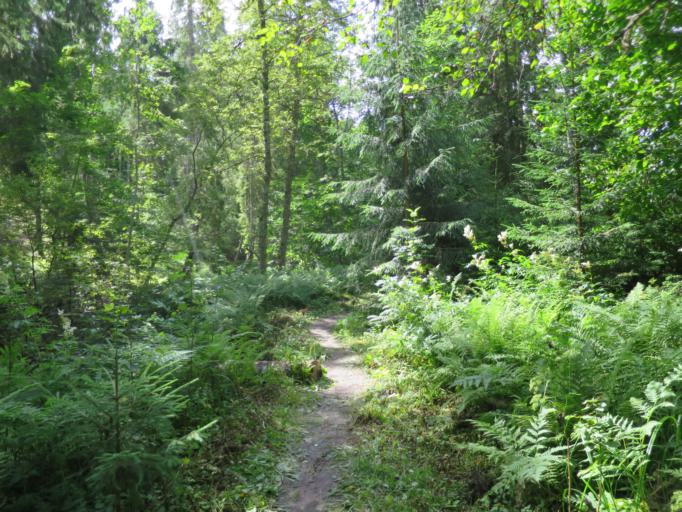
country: LV
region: Ligatne
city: Ligatne
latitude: 57.2211
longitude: 24.9679
